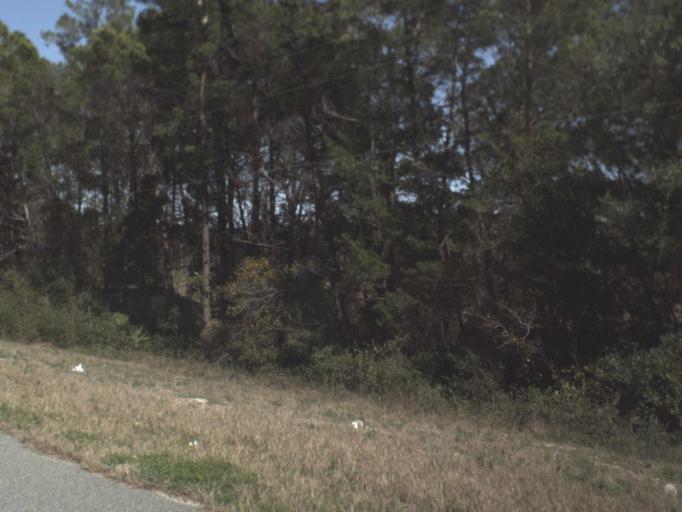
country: US
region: Florida
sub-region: Wakulla County
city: Crawfordville
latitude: 29.9250
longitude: -84.4024
